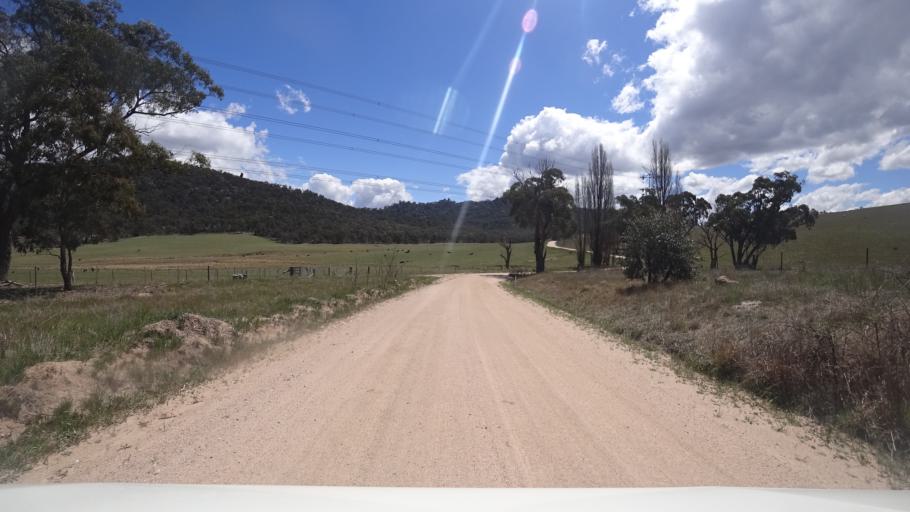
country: AU
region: New South Wales
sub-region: Oberon
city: Oberon
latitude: -33.5588
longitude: 149.9342
